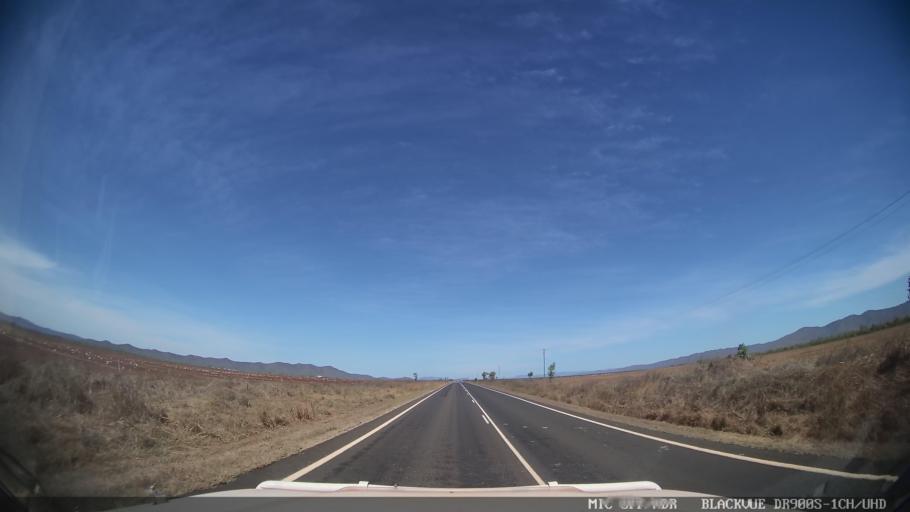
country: AU
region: Queensland
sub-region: Cook
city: Cooktown
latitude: -15.7927
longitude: 144.7100
